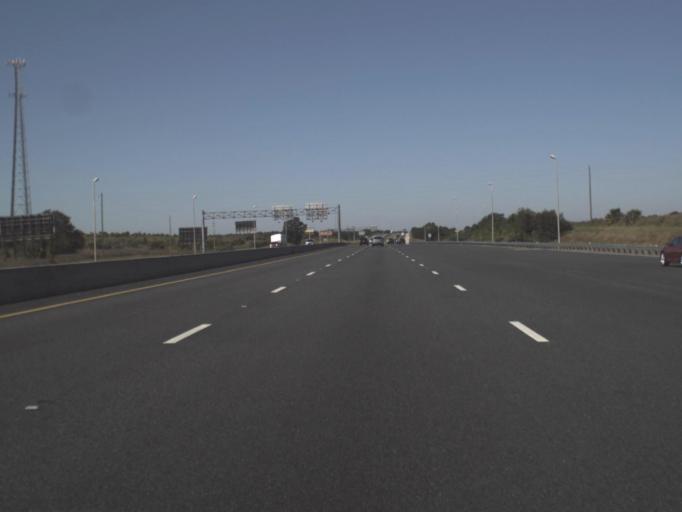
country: US
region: Florida
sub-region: Lake County
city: Yalaha
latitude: 28.6704
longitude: -81.8433
